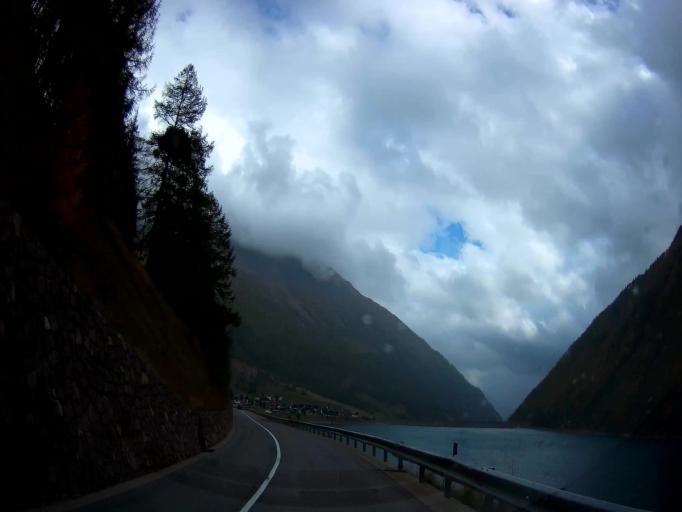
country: IT
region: Trentino-Alto Adige
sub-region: Bolzano
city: Senales
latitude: 46.7381
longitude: 10.8352
